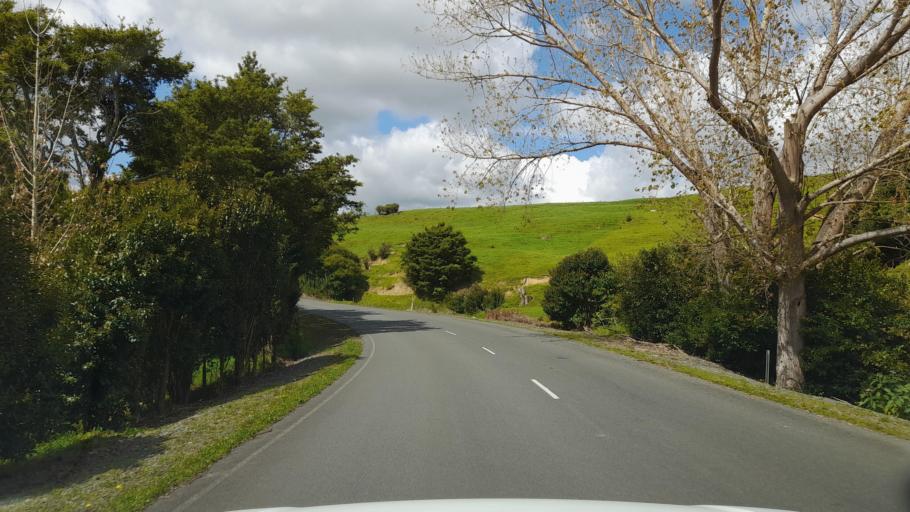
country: NZ
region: Northland
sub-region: Whangarei
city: Maungatapere
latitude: -35.6426
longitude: 174.0464
